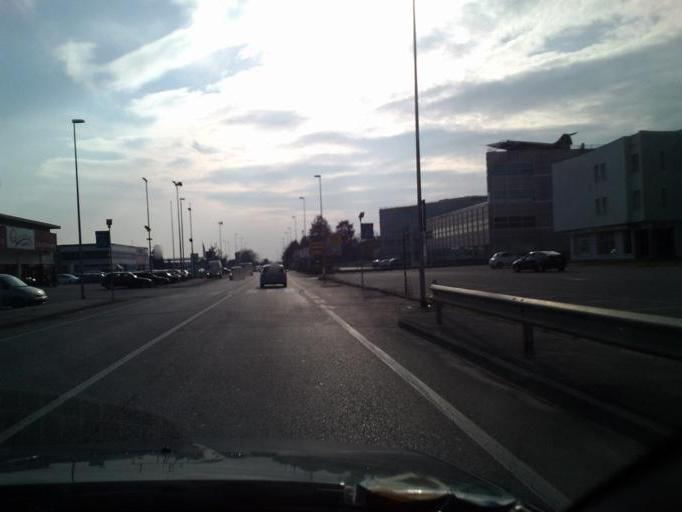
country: IT
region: Veneto
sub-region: Provincia di Verona
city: Villafranca di Verona
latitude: 45.3687
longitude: 10.8686
